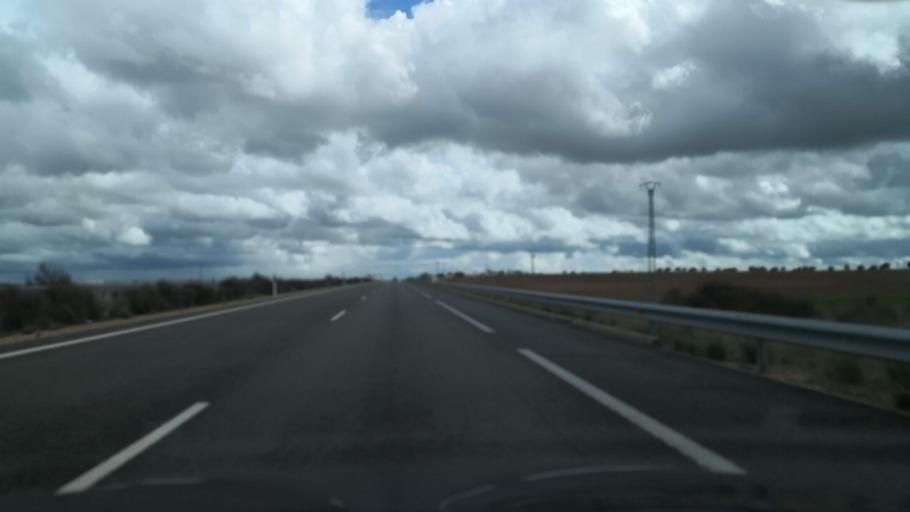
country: ES
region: Castille and Leon
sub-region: Provincia de Salamanca
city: Topas
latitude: 41.1929
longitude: -5.6982
